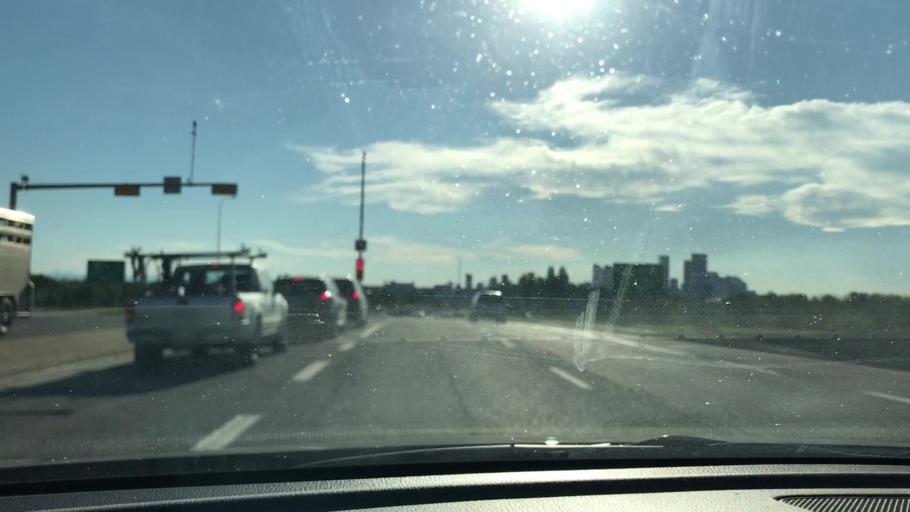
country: CA
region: Alberta
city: Calgary
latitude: 51.0372
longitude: -114.0061
